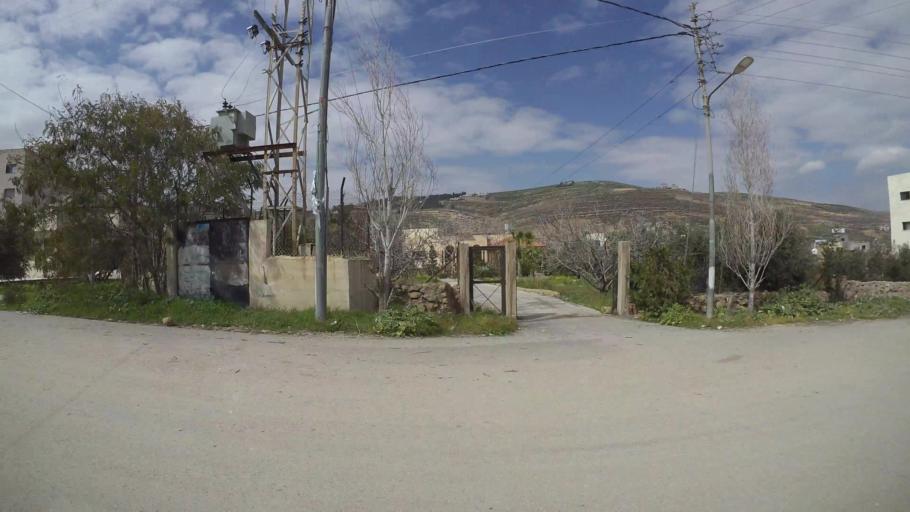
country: JO
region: Amman
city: Al Jubayhah
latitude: 32.0607
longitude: 35.8147
